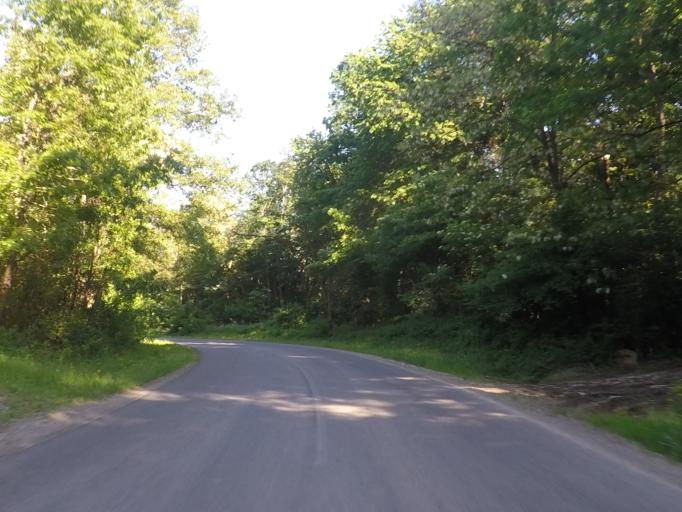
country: HU
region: Borsod-Abauj-Zemplen
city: Putnok
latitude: 48.4474
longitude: 20.4798
